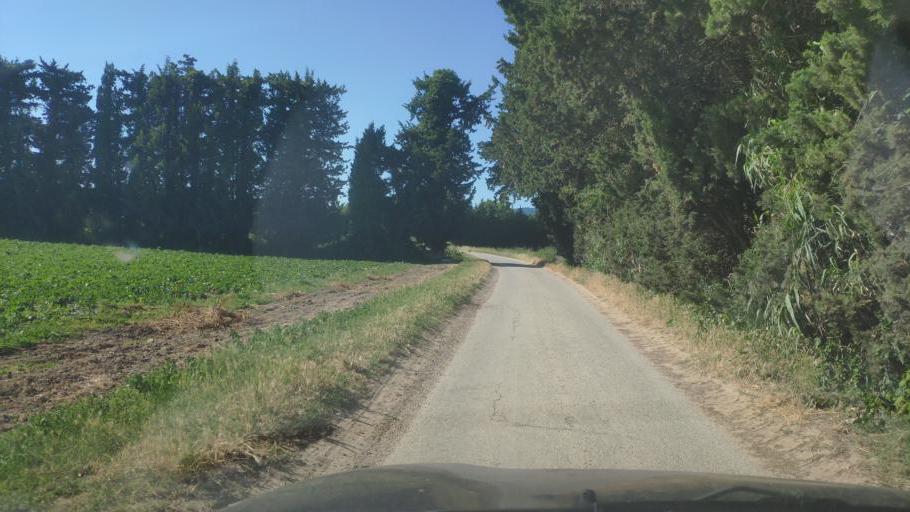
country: FR
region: Provence-Alpes-Cote d'Azur
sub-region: Departement du Vaucluse
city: Aubignan
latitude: 44.0819
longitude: 5.0203
